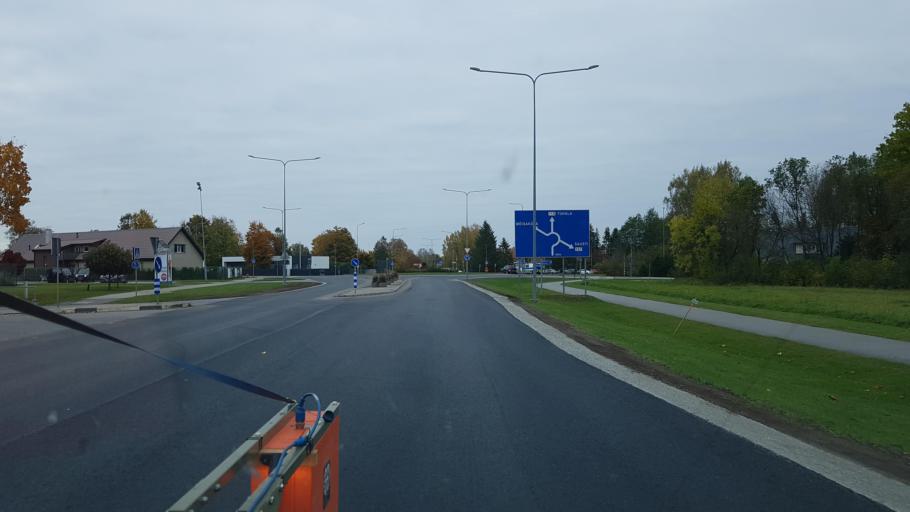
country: EE
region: Harju
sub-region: Kiili vald
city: Kiili
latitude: 59.3100
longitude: 24.8324
